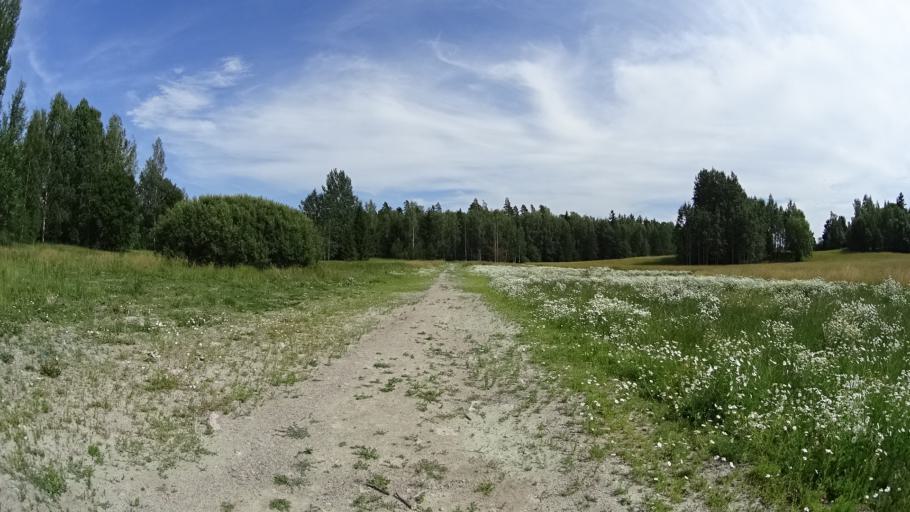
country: FI
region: Uusimaa
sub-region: Helsinki
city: Espoo
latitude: 60.1934
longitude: 24.6711
